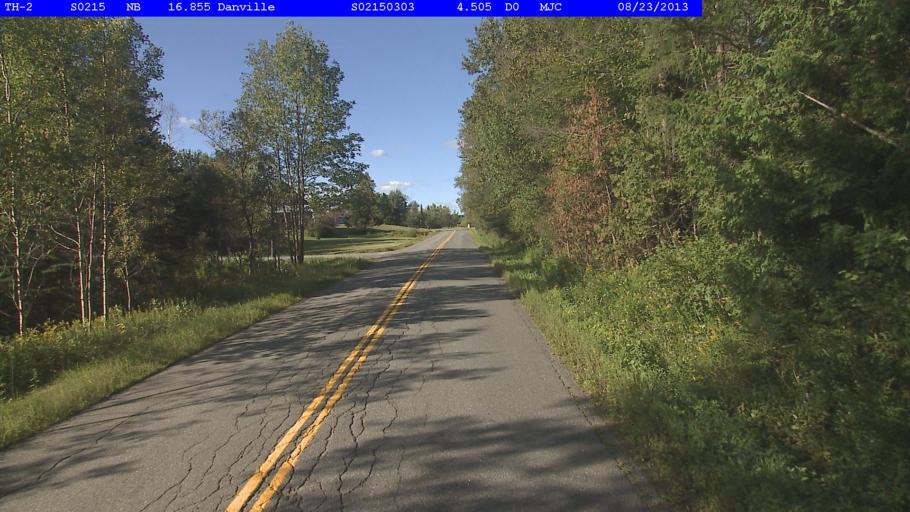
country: US
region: Vermont
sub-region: Caledonia County
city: St Johnsbury
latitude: 44.4288
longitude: -72.1414
